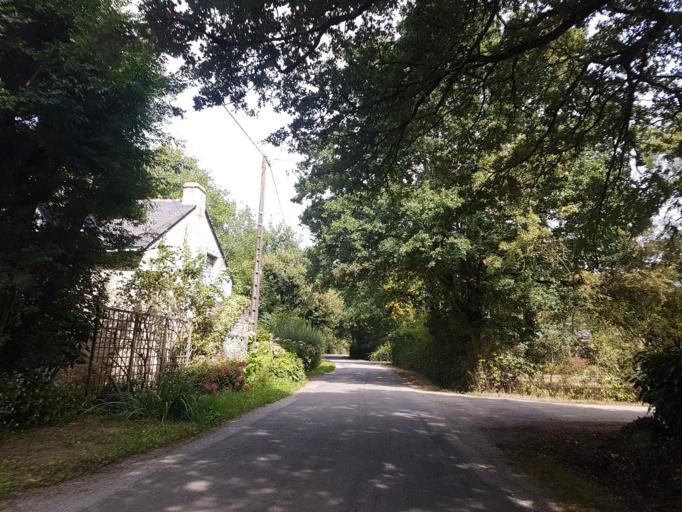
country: FR
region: Pays de la Loire
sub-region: Departement de la Loire-Atlantique
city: Petit-Mars
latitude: 47.3955
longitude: -1.4278
